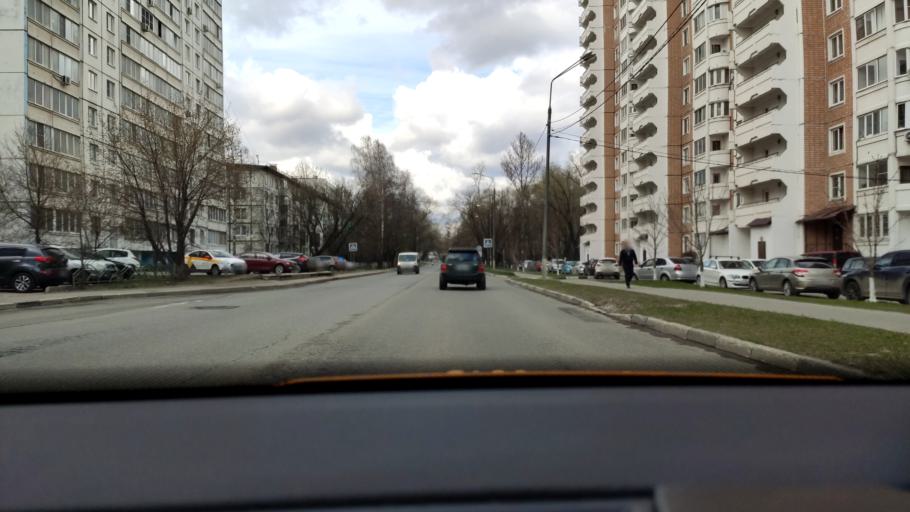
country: RU
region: Moskovskaya
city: Zheleznodorozhnyy
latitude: 55.7443
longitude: 38.0351
